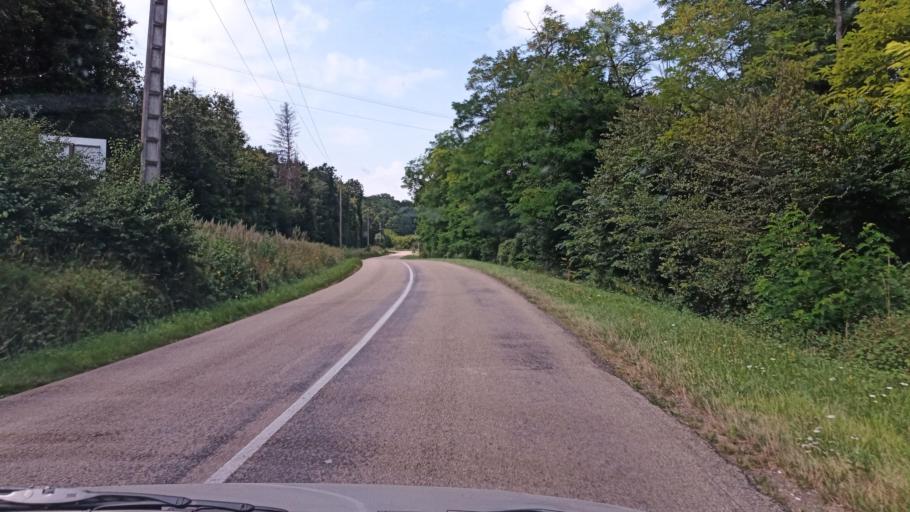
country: FR
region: Bourgogne
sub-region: Departement de l'Yonne
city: Villeneuve-sur-Yonne
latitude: 48.0767
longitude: 3.2739
